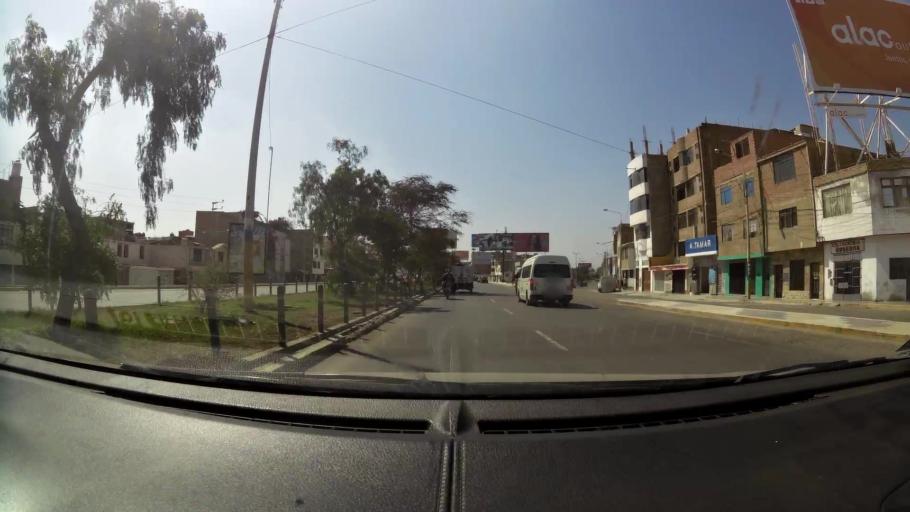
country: PE
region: Lambayeque
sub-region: Provincia de Chiclayo
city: Chiclayo
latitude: -6.7814
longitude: -79.8339
